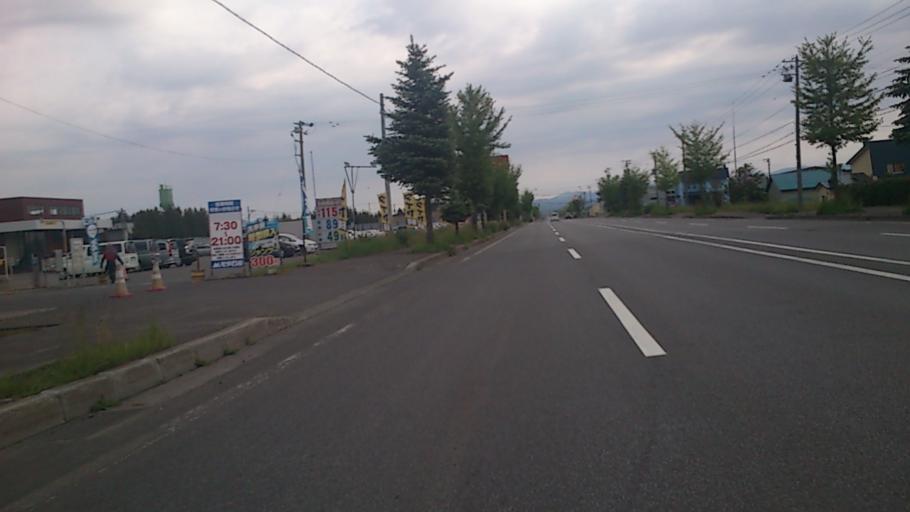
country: JP
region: Hokkaido
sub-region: Asahikawa-shi
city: Asahikawa
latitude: 43.8334
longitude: 142.4706
